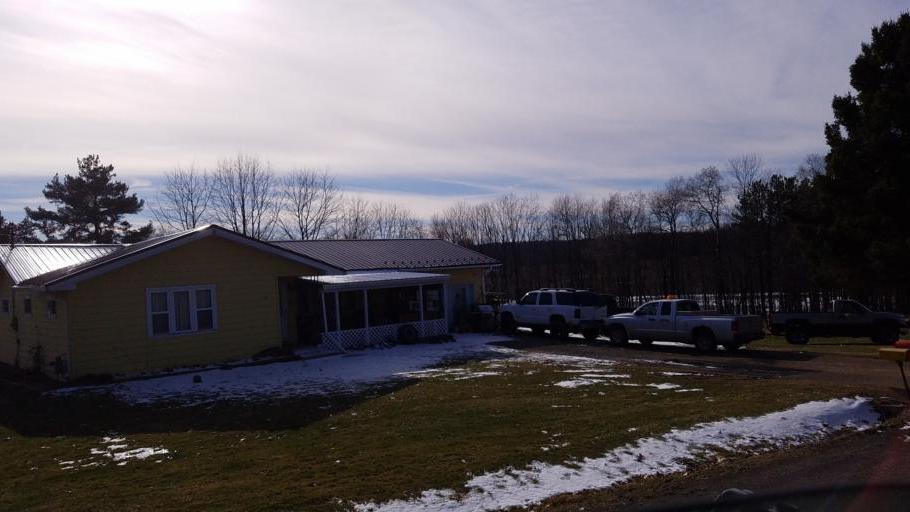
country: US
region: New York
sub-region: Allegany County
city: Wellsville
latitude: 42.0800
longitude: -78.0092
